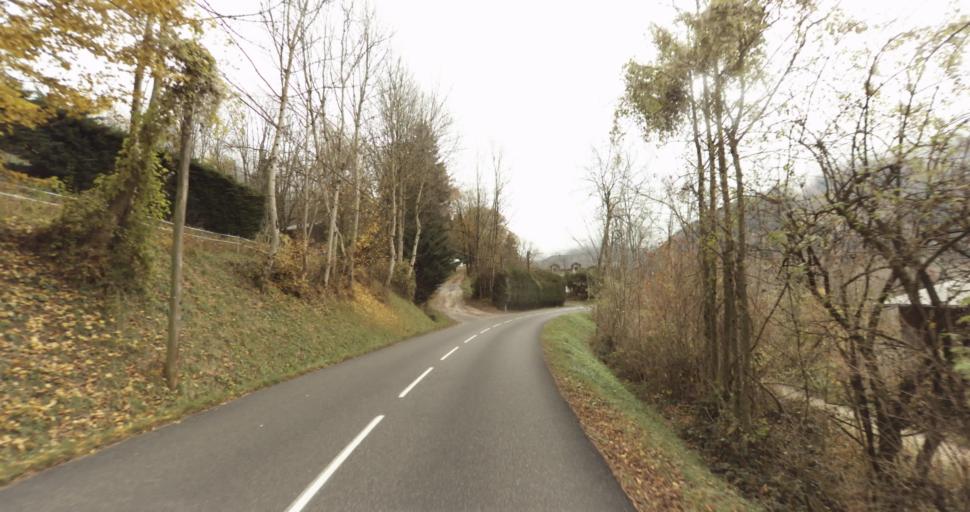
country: FR
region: Rhone-Alpes
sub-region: Departement de la Haute-Savoie
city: Thorens-Glieres
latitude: 45.9819
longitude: 6.2830
